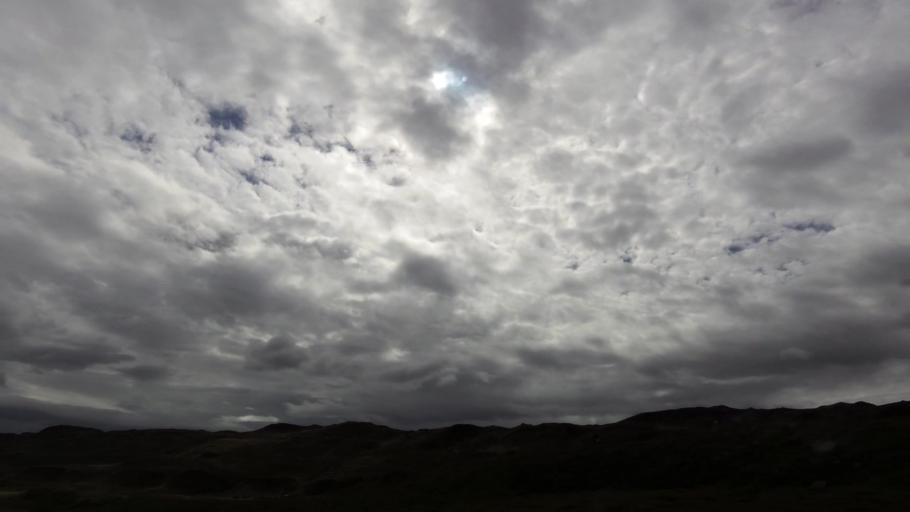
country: IS
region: West
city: Stykkisholmur
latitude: 65.5378
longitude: -22.1201
